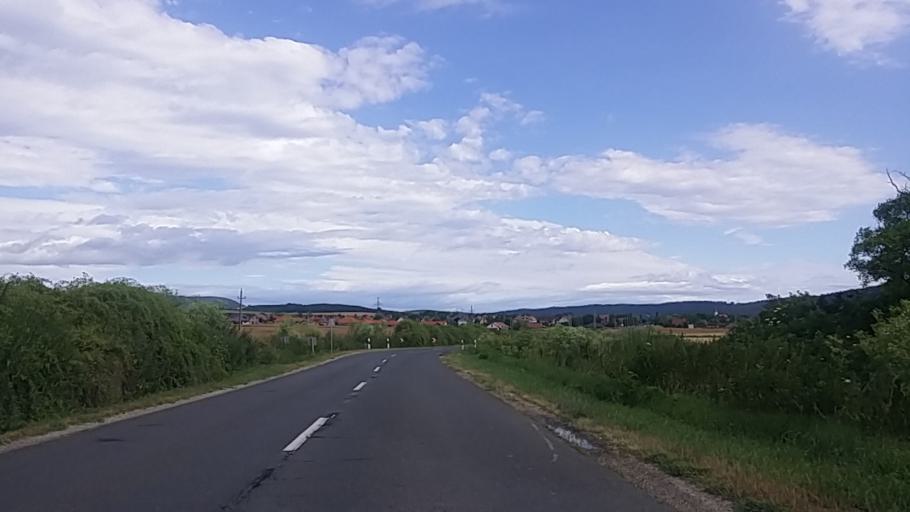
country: HU
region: Pest
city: Kosd
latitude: 47.7786
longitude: 19.2176
